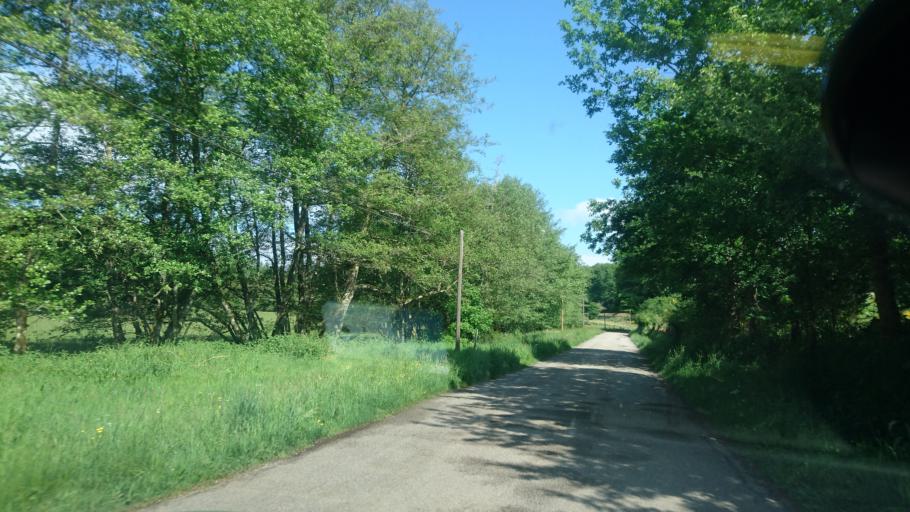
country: FR
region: Limousin
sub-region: Departement de la Haute-Vienne
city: Peyrat-le-Chateau
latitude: 45.8030
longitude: 1.7947
